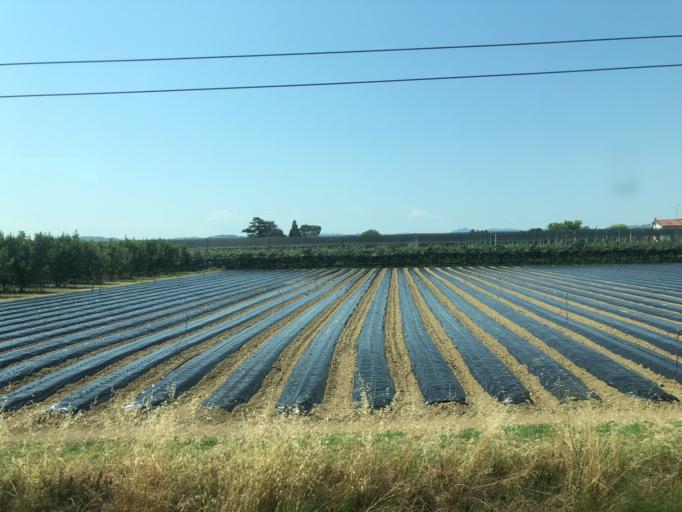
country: IT
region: Emilia-Romagna
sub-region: Provincia di Ravenna
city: Castel Bolognese
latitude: 44.3217
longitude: 11.8131
